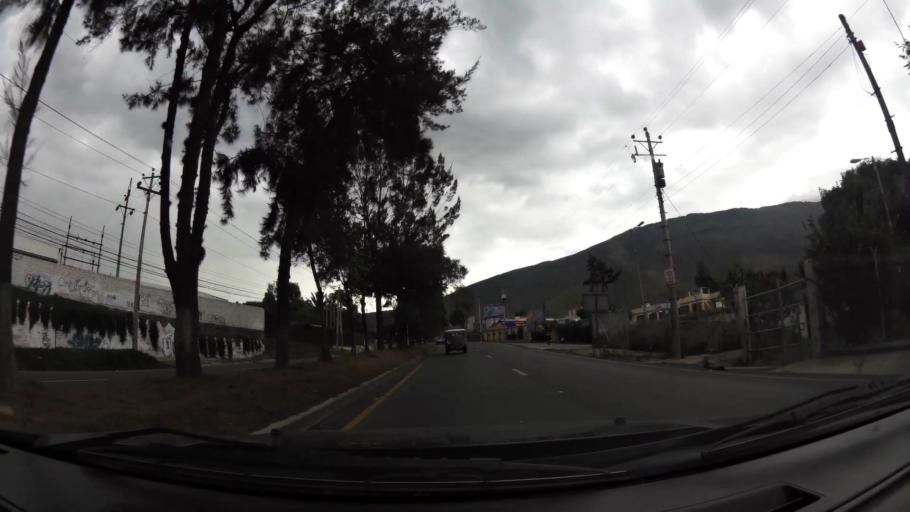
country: EC
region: Pichincha
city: Quito
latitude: -0.0657
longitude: -78.4620
